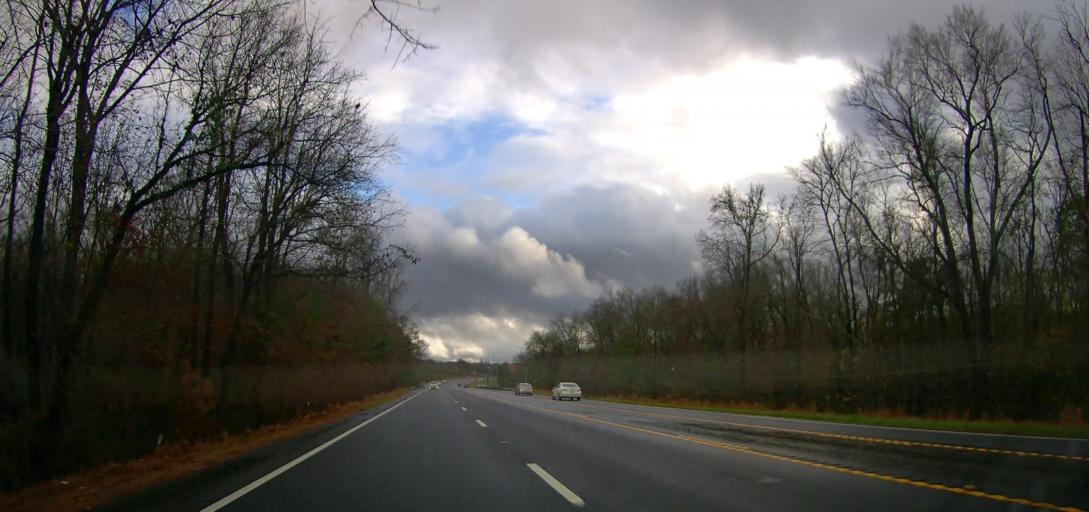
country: US
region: Georgia
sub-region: Clarke County
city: Athens
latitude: 33.9880
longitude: -83.3778
